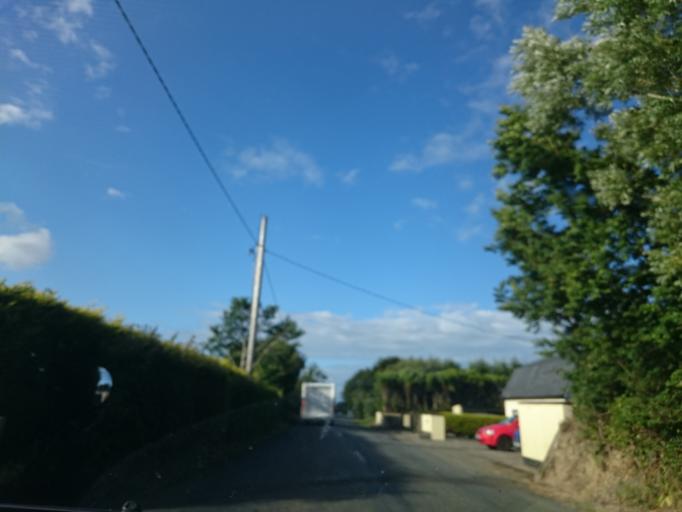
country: IE
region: Leinster
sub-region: Loch Garman
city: Loch Garman
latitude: 52.2239
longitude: -6.5076
